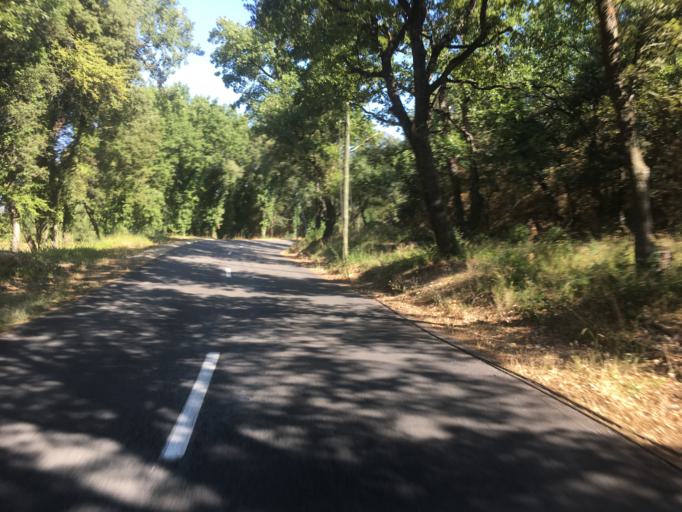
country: FR
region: Provence-Alpes-Cote d'Azur
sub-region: Departement des Alpes-de-Haute-Provence
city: Volx
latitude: 43.8241
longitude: 5.8546
